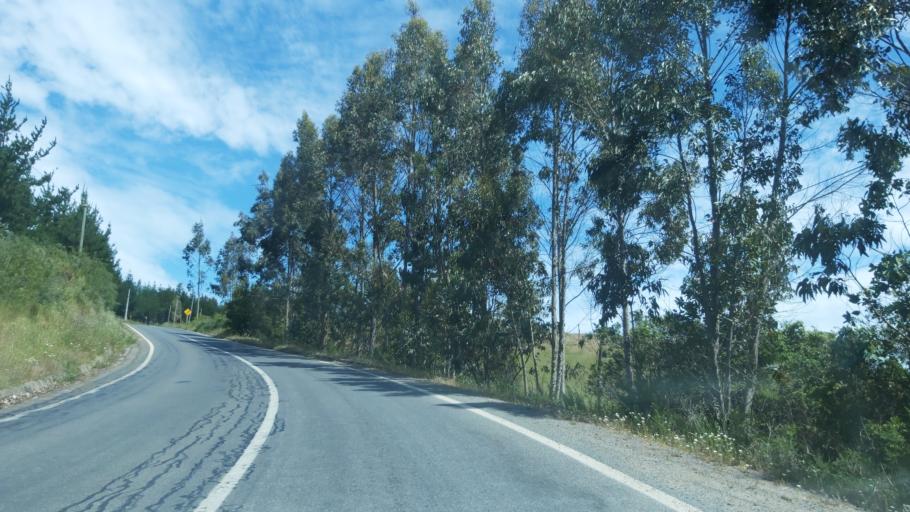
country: CL
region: Maule
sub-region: Provincia de Talca
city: Constitucion
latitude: -35.5702
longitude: -72.6036
